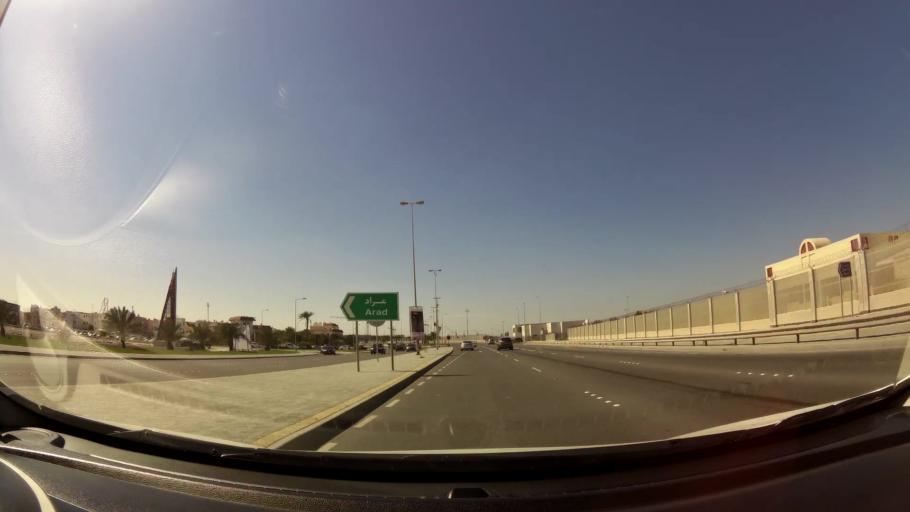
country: BH
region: Muharraq
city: Al Hadd
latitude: 26.2610
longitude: 50.6424
